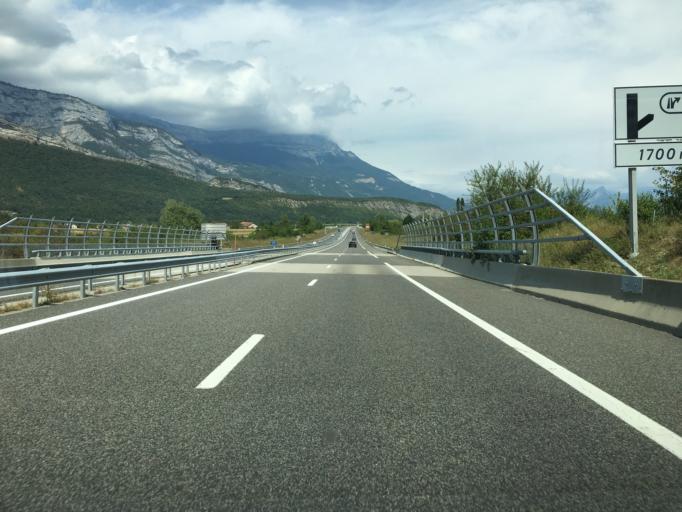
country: FR
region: Rhone-Alpes
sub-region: Departement de l'Isere
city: Vif
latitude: 45.0575
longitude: 5.6855
